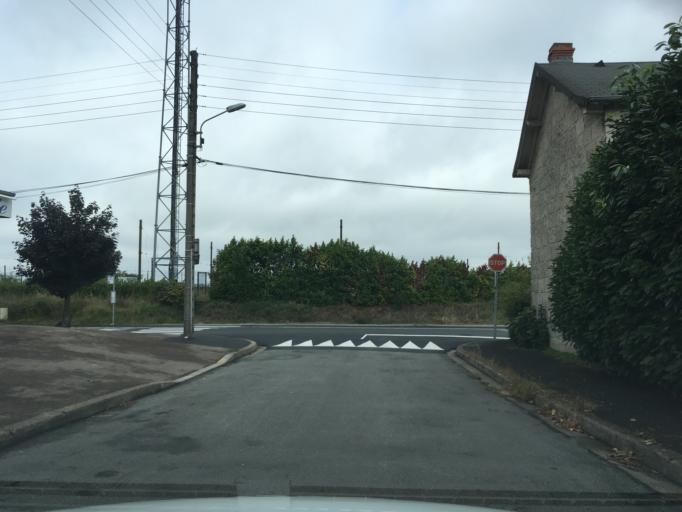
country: FR
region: Limousin
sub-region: Departement de la Correze
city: Brive-la-Gaillarde
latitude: 45.1483
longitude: 1.5105
